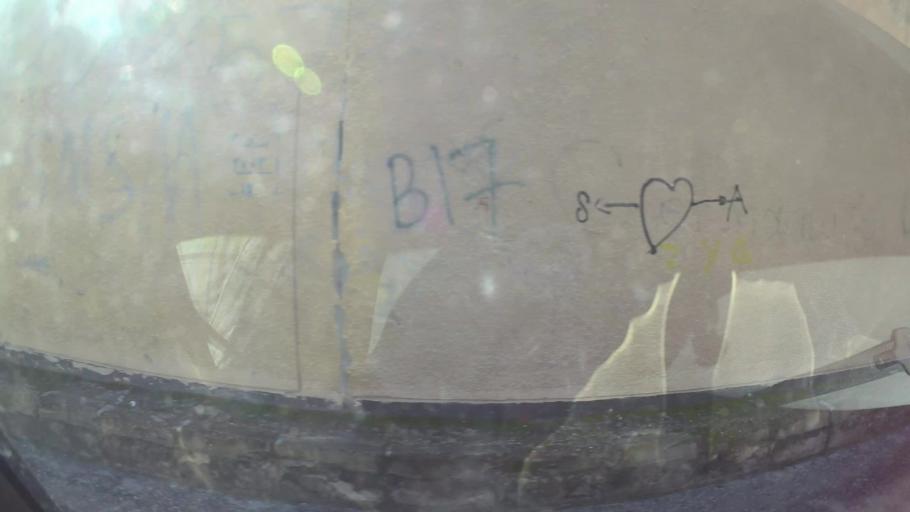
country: JO
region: Amman
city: Al Jubayhah
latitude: 32.0575
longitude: 35.8826
